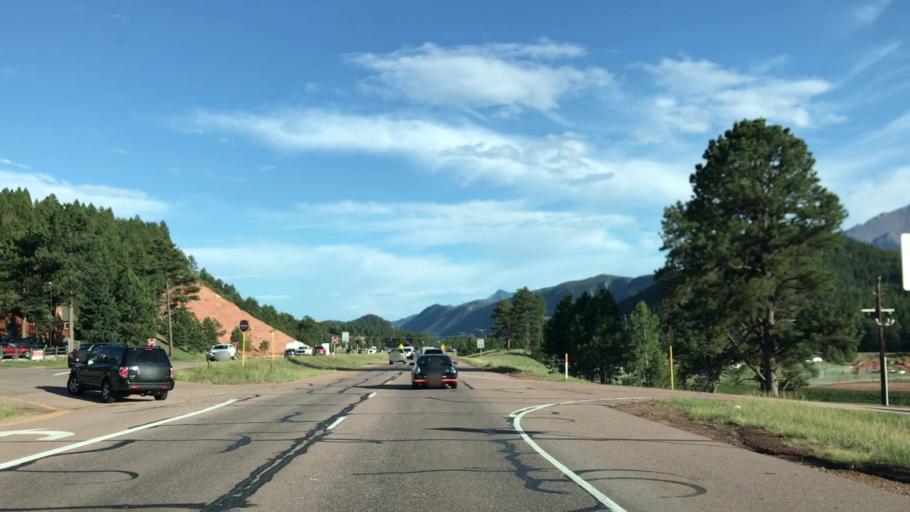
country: US
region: Colorado
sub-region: Teller County
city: Woodland Park
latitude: 38.9788
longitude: -105.0419
